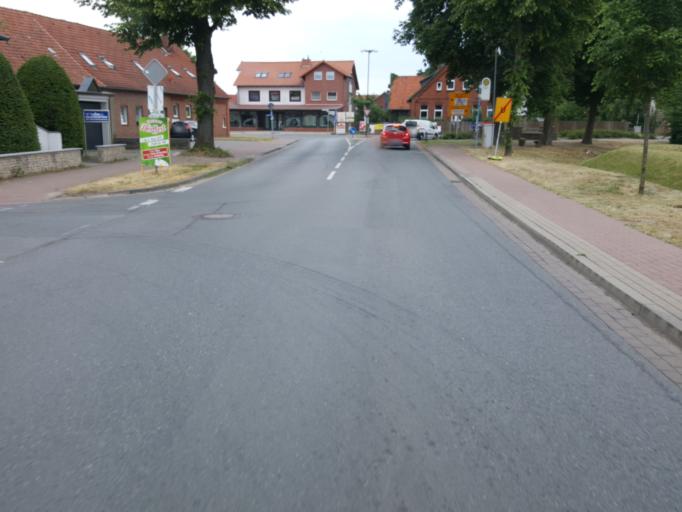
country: DE
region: Lower Saxony
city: Rehburg-Loccum
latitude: 52.4700
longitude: 9.2246
